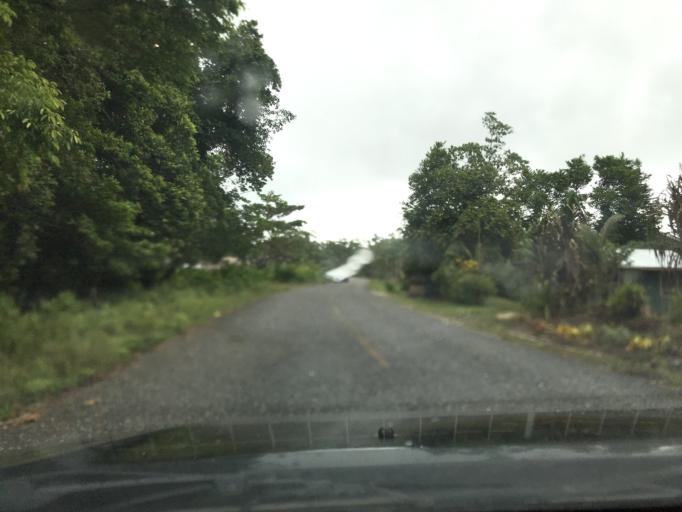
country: SB
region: Western Province
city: Gizo
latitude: -8.3206
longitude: 157.2565
